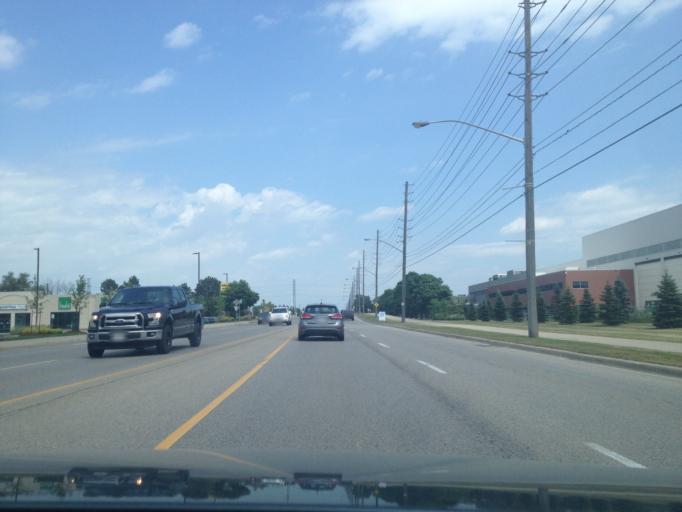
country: CA
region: Ontario
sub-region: Wellington County
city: Guelph
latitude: 43.5537
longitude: -80.2929
